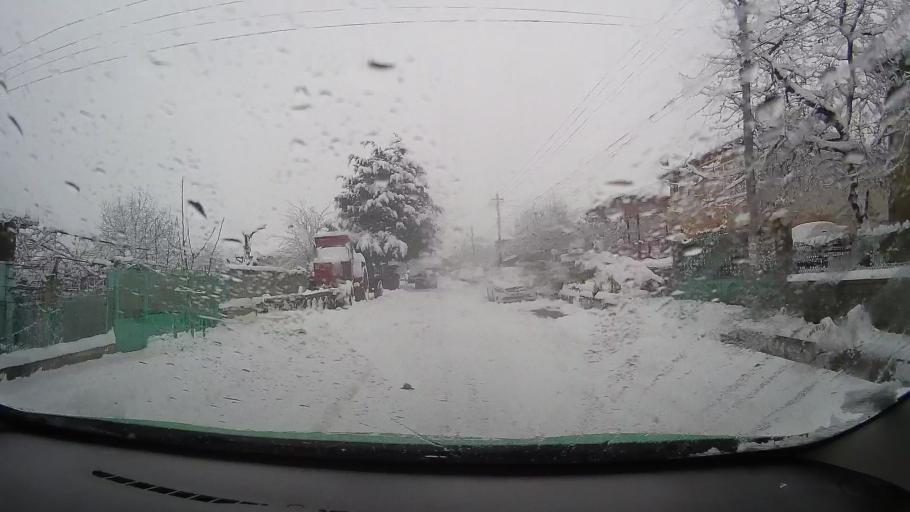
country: RO
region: Hunedoara
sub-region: Comuna Teliucu Inferior
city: Teliucu Inferior
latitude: 45.7003
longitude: 22.8932
